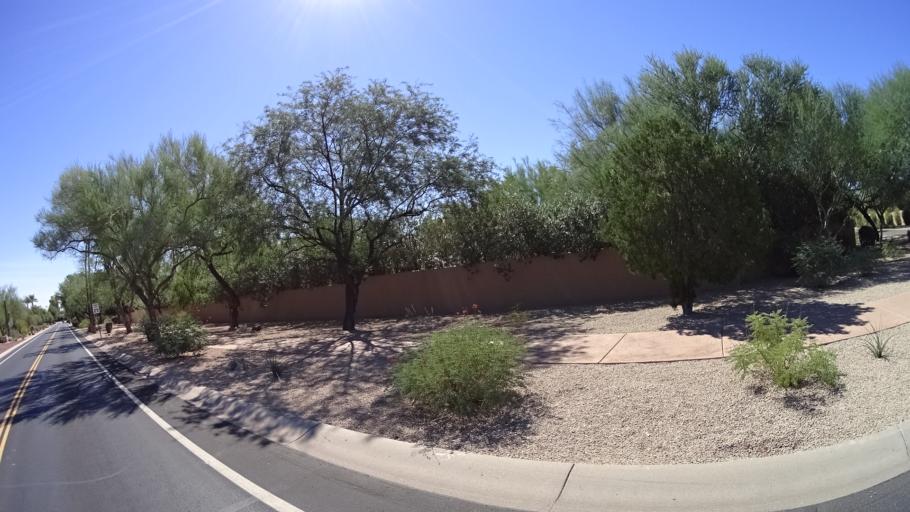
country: US
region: Arizona
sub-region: Maricopa County
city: Paradise Valley
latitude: 33.5459
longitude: -111.9301
